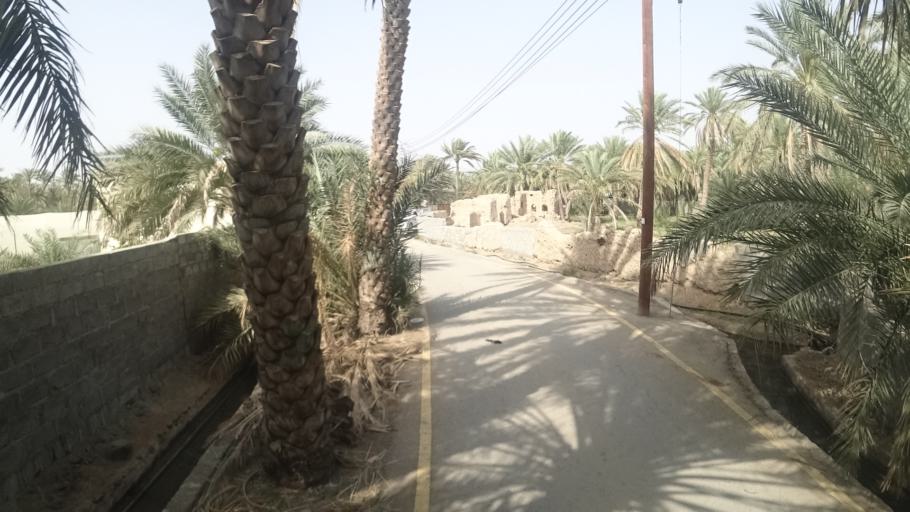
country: OM
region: Ash Sharqiyah
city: Ibra'
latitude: 22.7117
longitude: 58.1714
